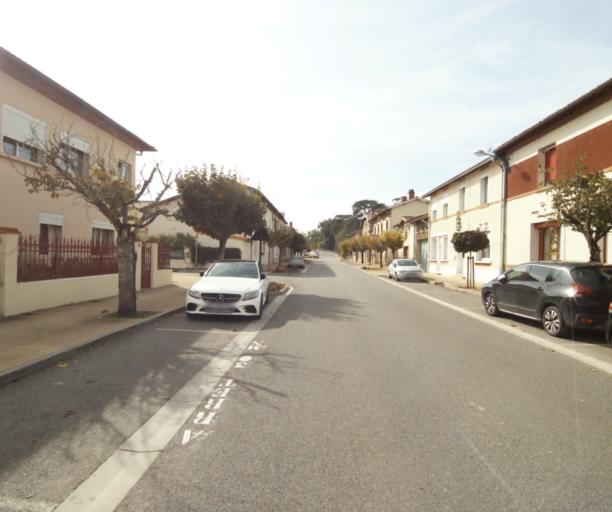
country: FR
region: Midi-Pyrenees
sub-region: Departement du Tarn-et-Garonne
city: Orgueil
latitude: 43.9174
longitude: 1.3981
